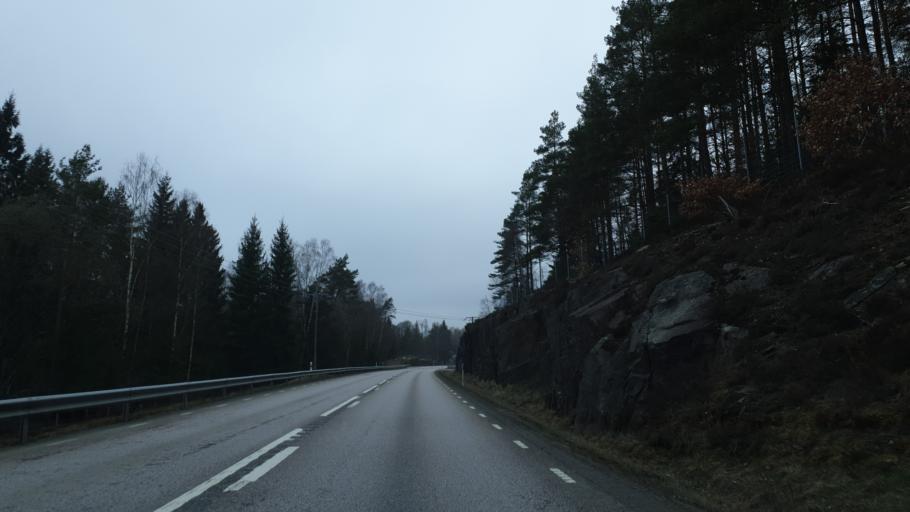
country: SE
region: Vaestra Goetaland
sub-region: Harryda Kommun
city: Hindas
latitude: 57.6326
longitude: 12.4110
